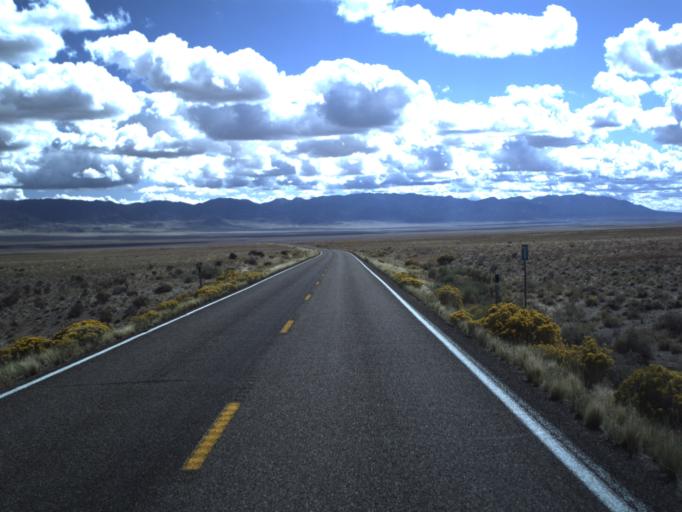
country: US
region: Utah
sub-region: Beaver County
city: Milford
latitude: 38.5835
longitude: -113.8114
